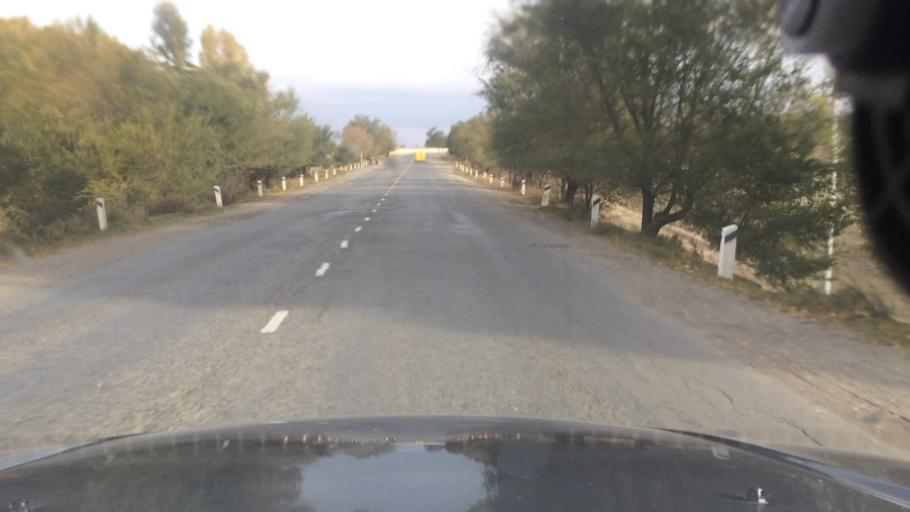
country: KG
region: Ysyk-Koel
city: Karakol
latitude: 42.5340
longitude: 78.3818
